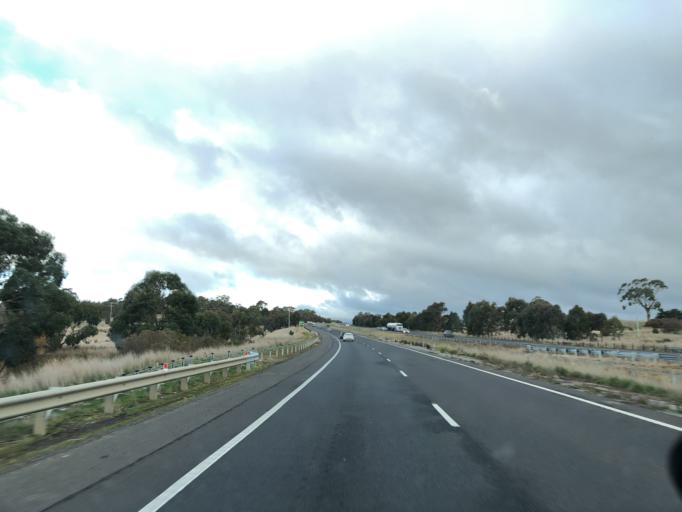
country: AU
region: Victoria
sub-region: Mount Alexander
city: Castlemaine
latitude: -37.2710
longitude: 144.4788
